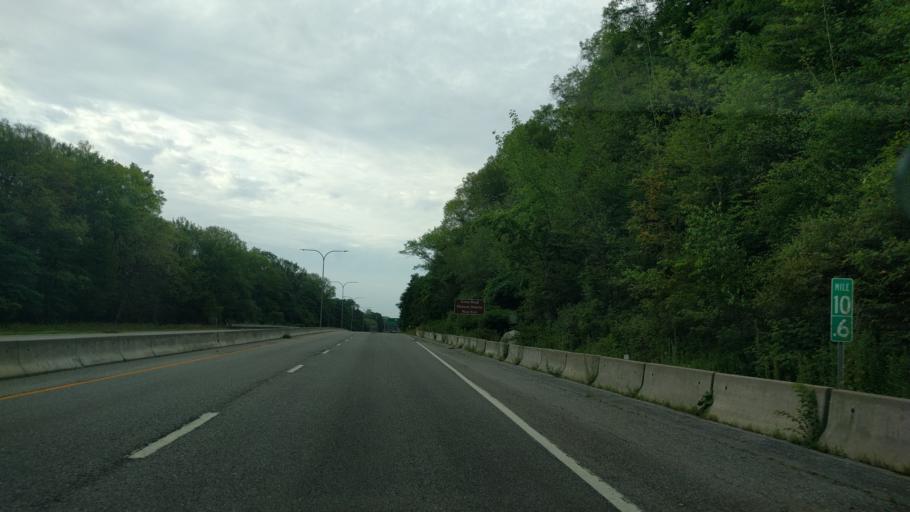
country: US
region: Rhode Island
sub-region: Providence County
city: Valley Falls
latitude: 41.9079
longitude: -71.4500
